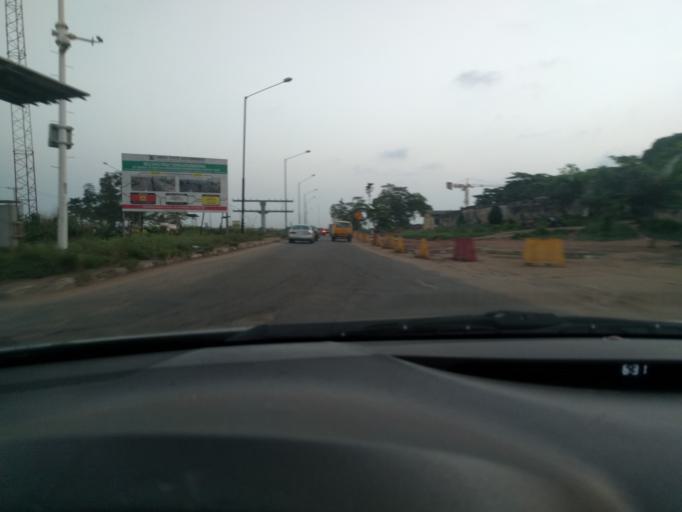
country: NG
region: Lagos
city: Oshodi
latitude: 6.5616
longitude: 3.3212
